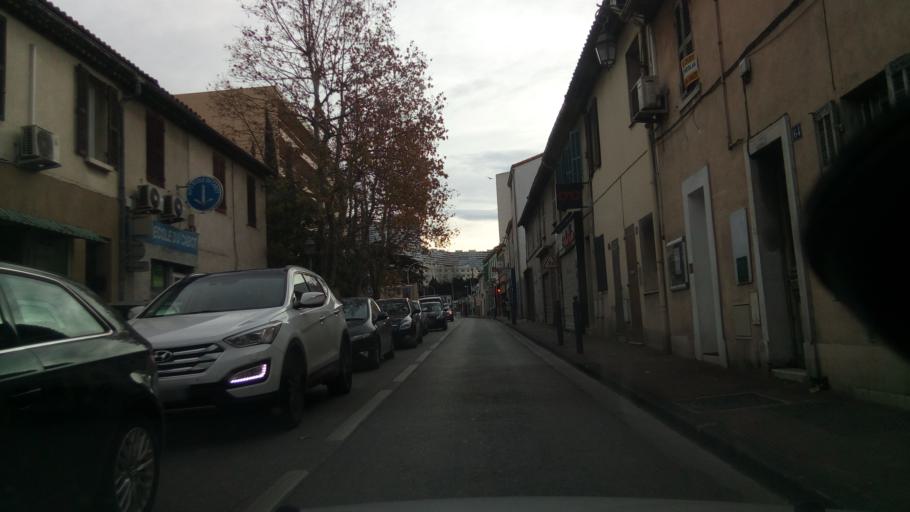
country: FR
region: Provence-Alpes-Cote d'Azur
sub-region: Departement des Bouches-du-Rhone
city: Marseille 09
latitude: 43.2585
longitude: 5.4178
